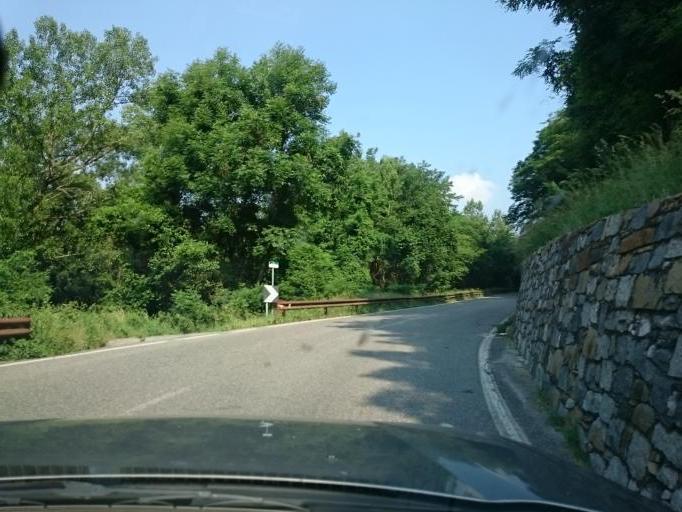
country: IT
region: Lombardy
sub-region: Provincia di Brescia
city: Cimbergo
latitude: 46.0174
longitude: 10.3578
